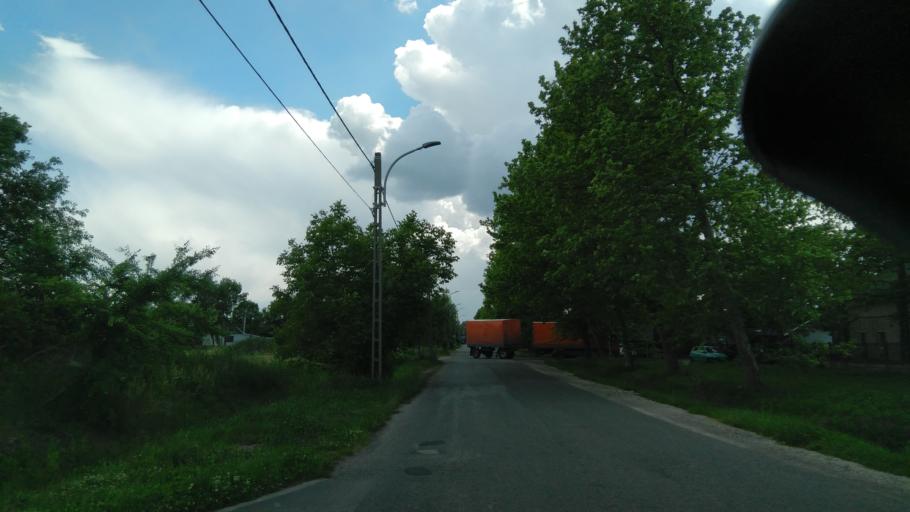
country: HU
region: Bekes
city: Gyula
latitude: 46.6620
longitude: 21.2696
